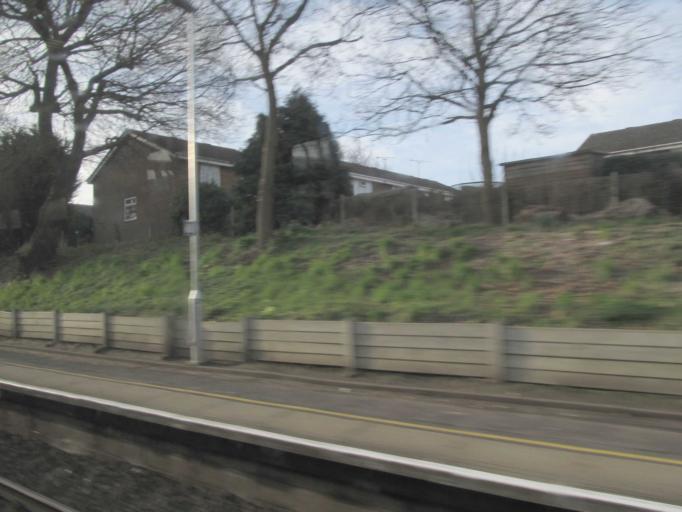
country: GB
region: England
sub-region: Wokingham
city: Winnersh
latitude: 51.4316
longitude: -0.8797
